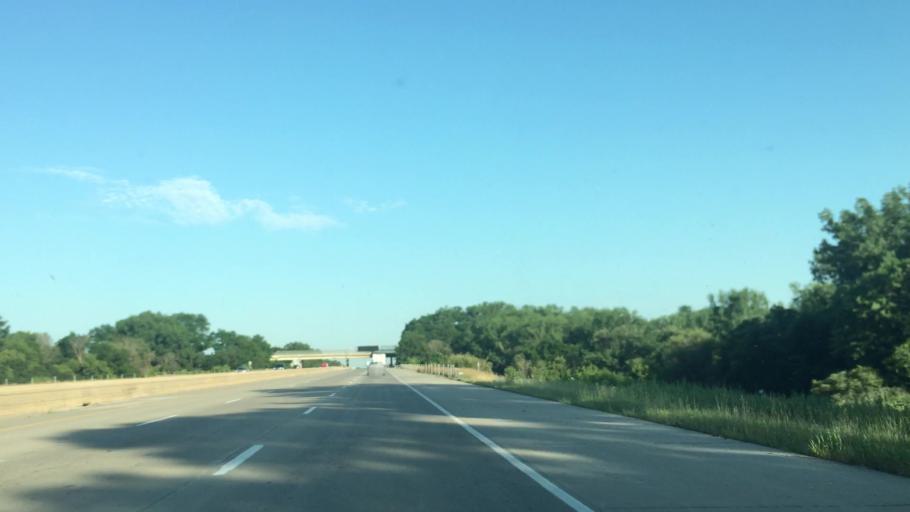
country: US
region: Iowa
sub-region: Johnson County
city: Coralville
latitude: 41.6880
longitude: -91.5772
